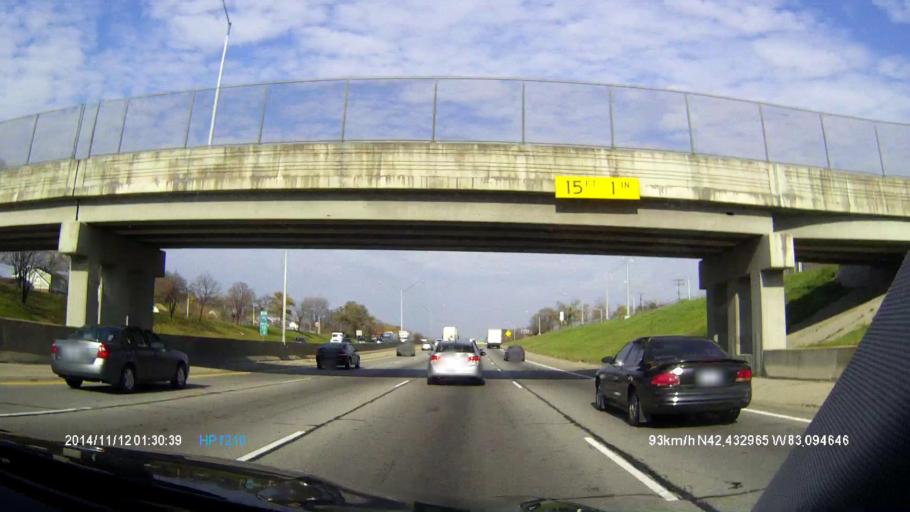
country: US
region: Michigan
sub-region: Wayne County
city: Highland Park
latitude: 42.4328
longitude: -83.0946
